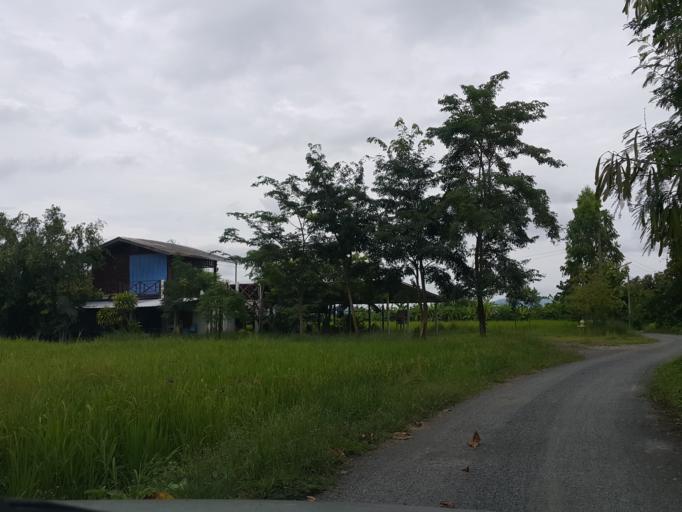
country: TH
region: Chiang Mai
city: San Sai
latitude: 18.8337
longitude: 99.1183
